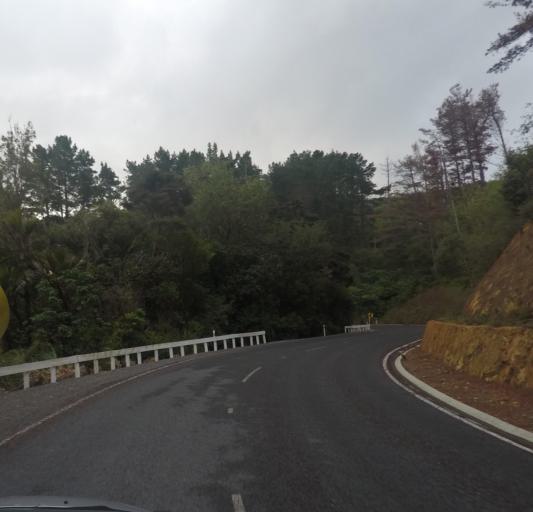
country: NZ
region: Auckland
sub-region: Auckland
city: Warkworth
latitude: -36.3749
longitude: 174.8020
